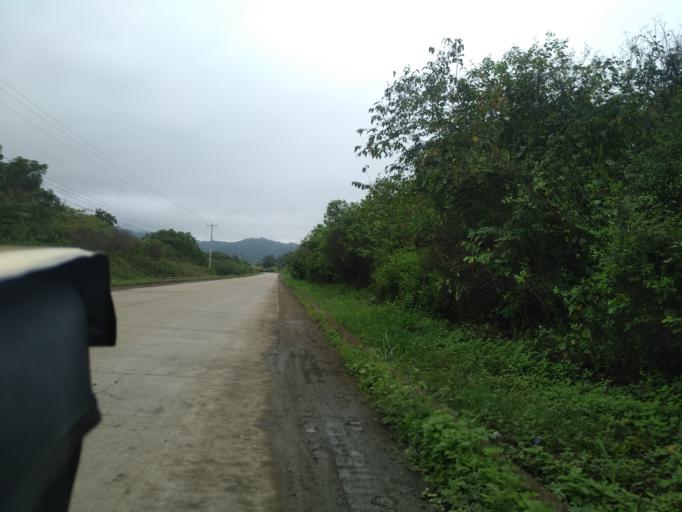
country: EC
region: Manabi
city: Jipijapa
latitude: -1.6611
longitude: -80.8162
